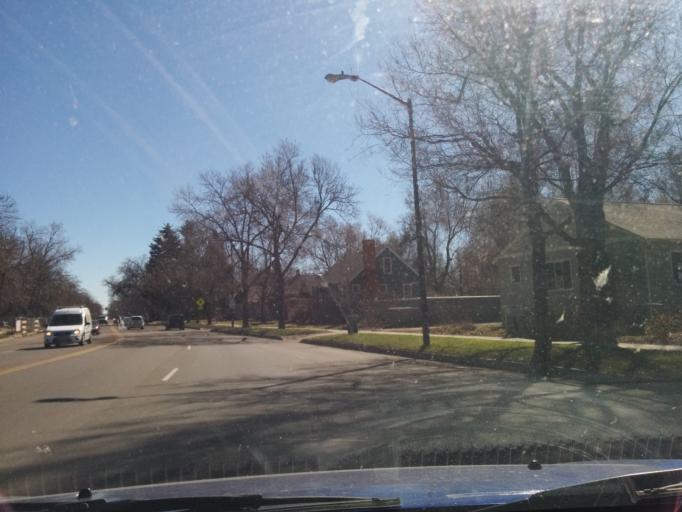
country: US
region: Colorado
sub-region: Larimer County
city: Fort Collins
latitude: 40.5815
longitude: -105.0861
